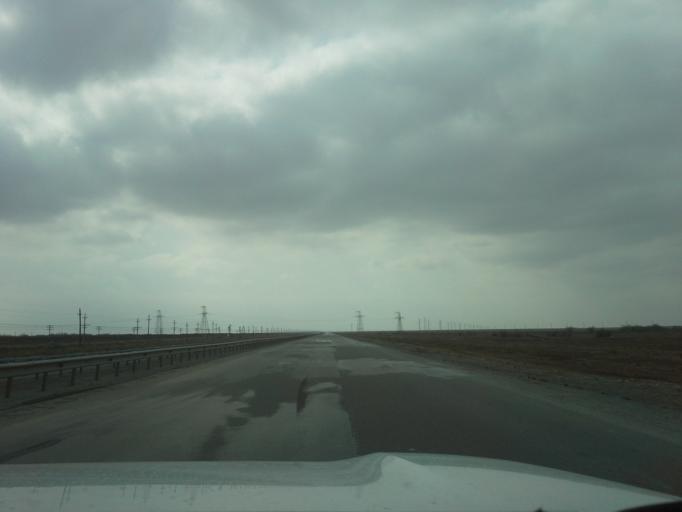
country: IR
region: Razavi Khorasan
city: Kalat-e Naderi
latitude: 37.2168
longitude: 60.0996
